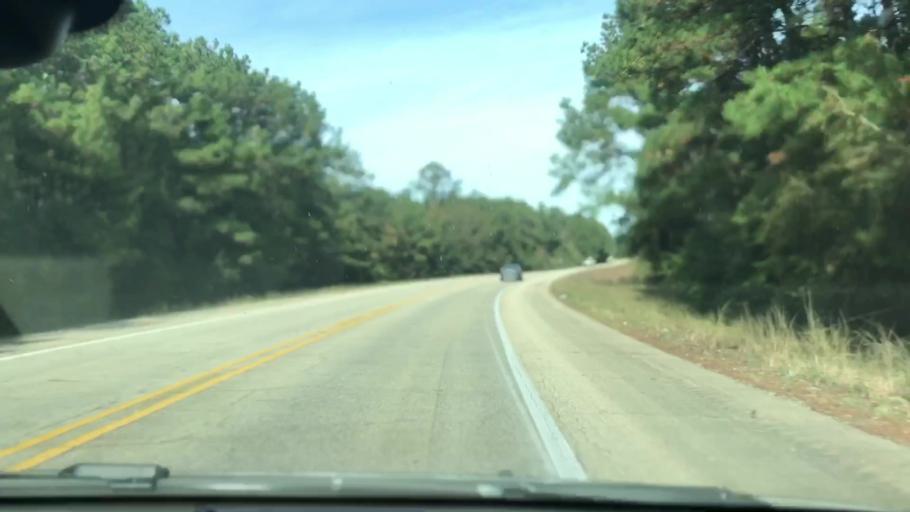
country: US
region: Louisiana
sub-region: Saint Tammany Parish
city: Pearl River
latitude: 30.4734
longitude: -89.8126
